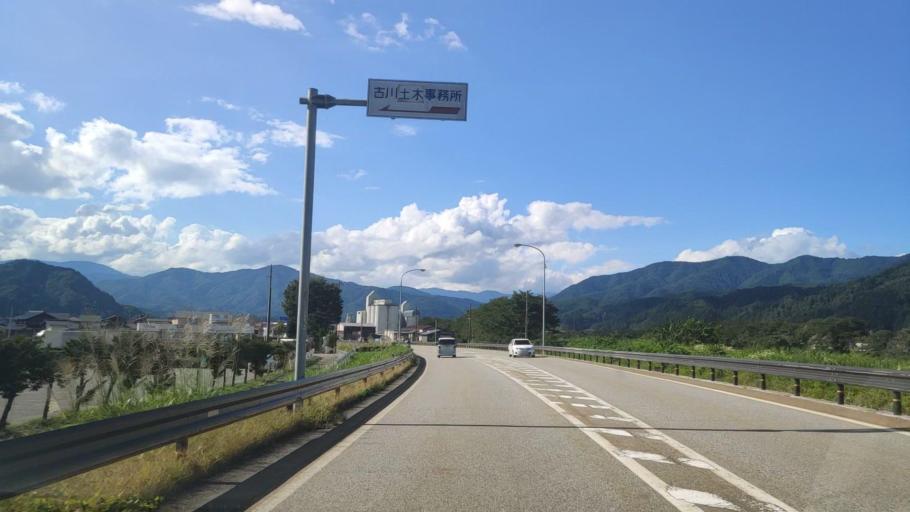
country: JP
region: Gifu
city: Takayama
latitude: 36.2449
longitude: 137.1707
